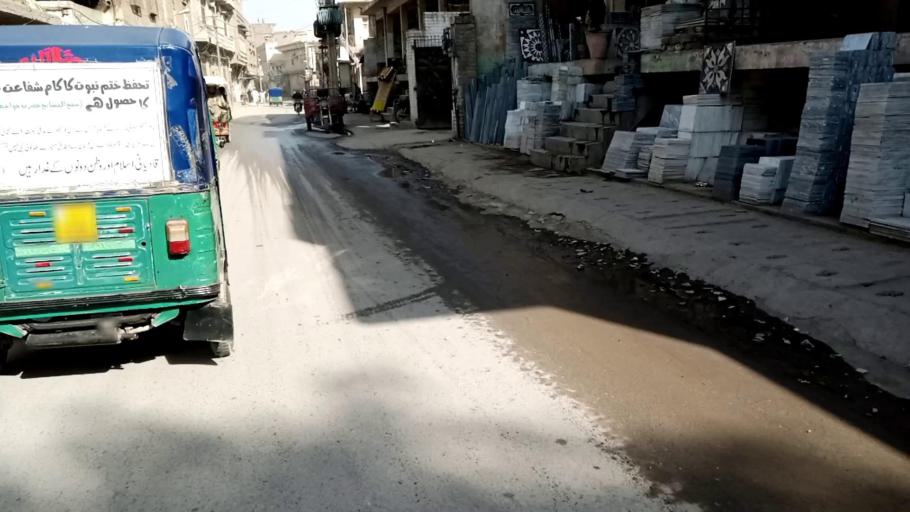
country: PK
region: Khyber Pakhtunkhwa
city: Peshawar
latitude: 33.9999
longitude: 71.5784
